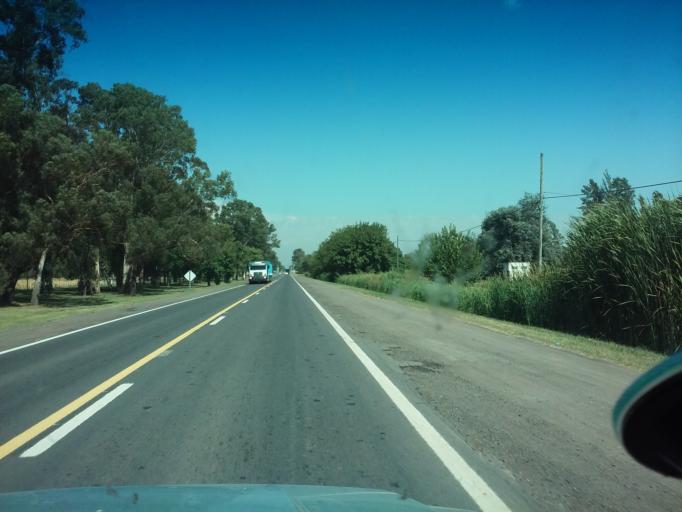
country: AR
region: Buenos Aires
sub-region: Partido de Nueve de Julio
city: Nueve de Julio
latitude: -35.4845
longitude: -60.8814
